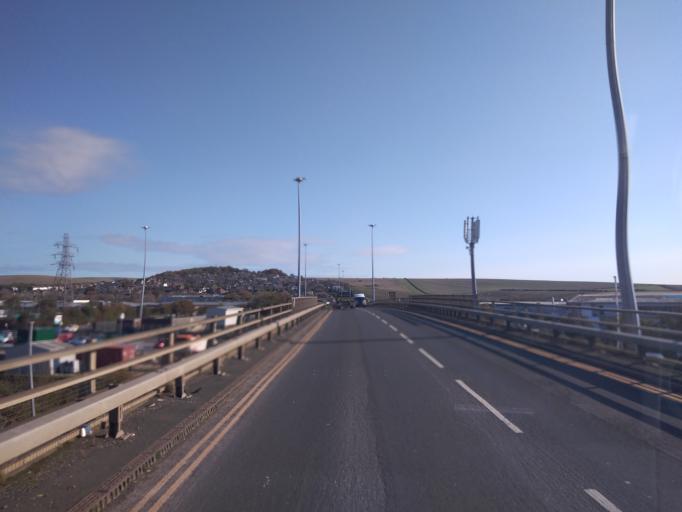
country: GB
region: England
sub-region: East Sussex
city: Newhaven
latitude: 50.7956
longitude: 0.0543
